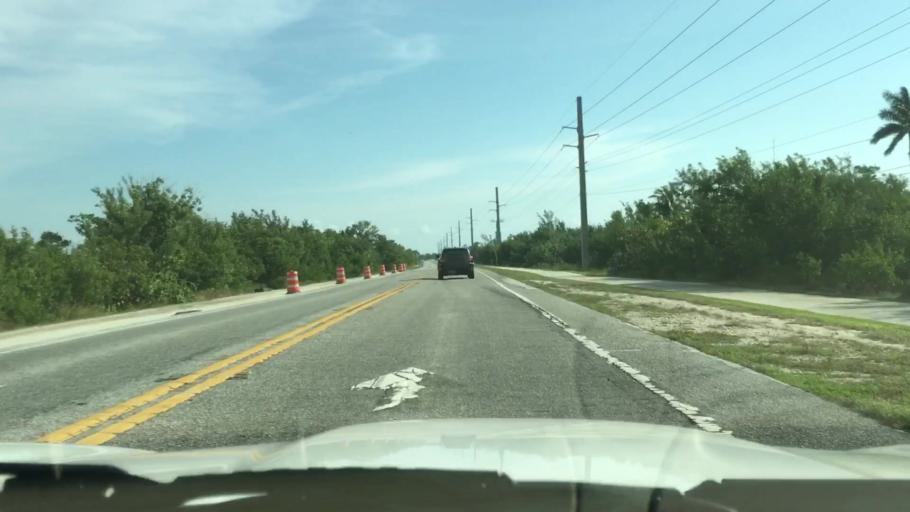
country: US
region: Florida
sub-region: Monroe County
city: Cudjoe Key
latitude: 24.6632
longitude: -81.5113
